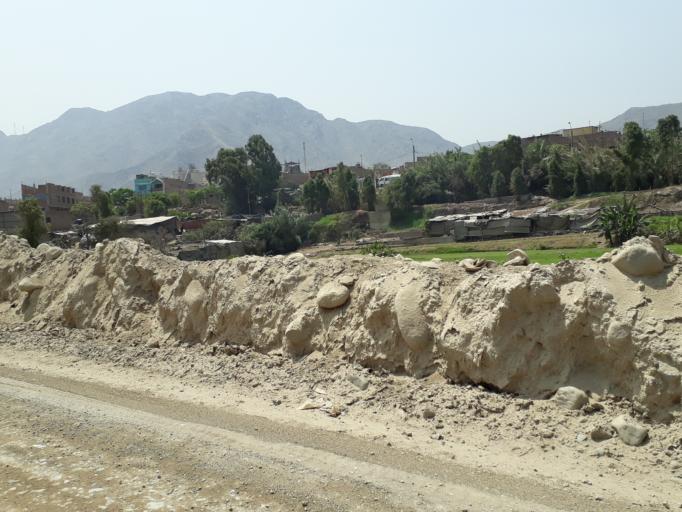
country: PE
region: Lima
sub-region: Lima
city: Santa Maria
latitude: -11.9913
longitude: -76.9044
